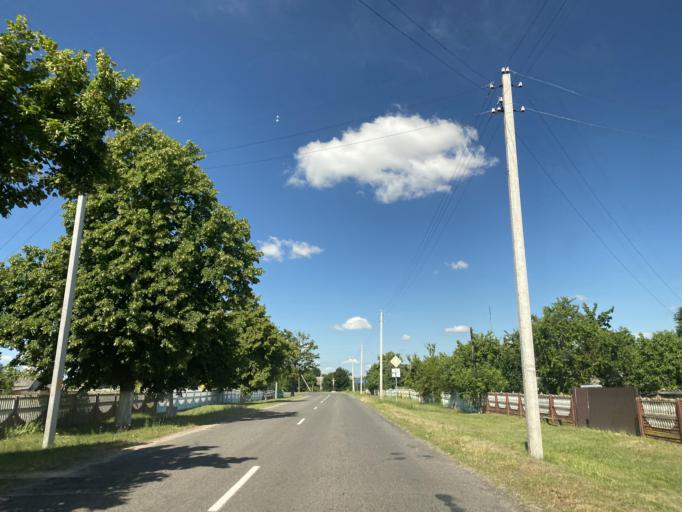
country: BY
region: Brest
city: Ivanava
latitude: 52.2341
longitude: 25.6547
